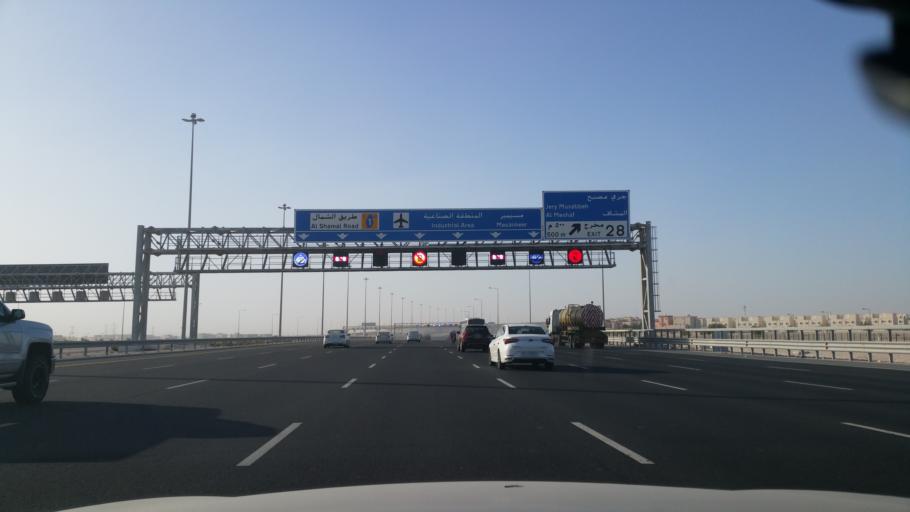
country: QA
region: Al Wakrah
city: Al Wukayr
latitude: 25.1733
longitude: 51.5565
